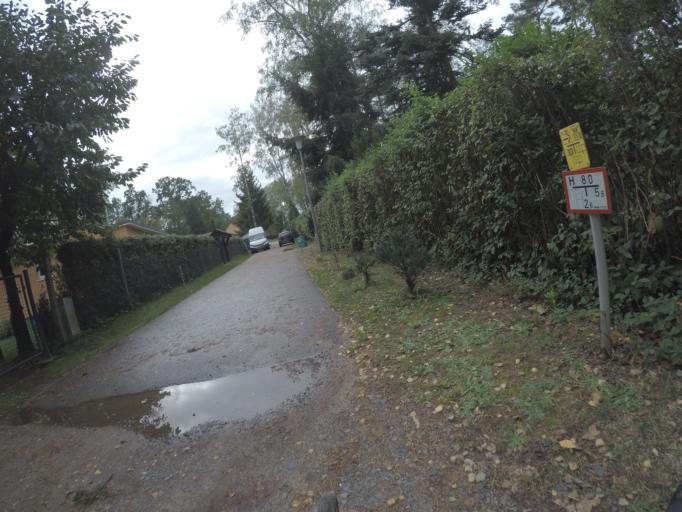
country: DE
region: Berlin
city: Buch
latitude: 52.6824
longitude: 13.4744
